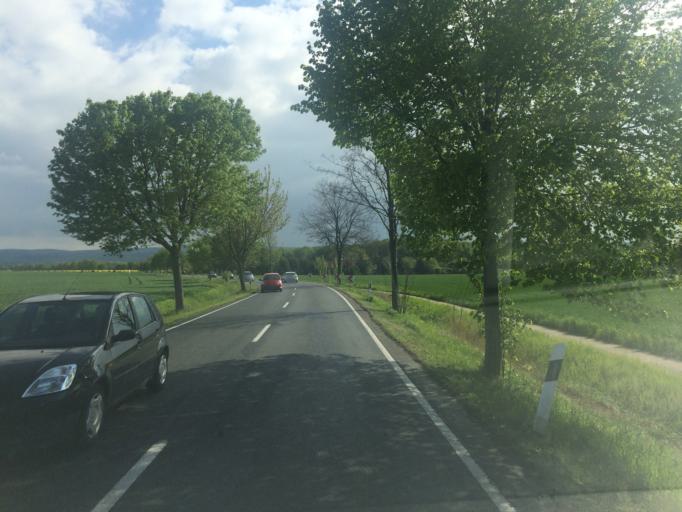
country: DE
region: Lower Saxony
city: Gross Munzel
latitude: 52.3467
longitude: 9.4630
